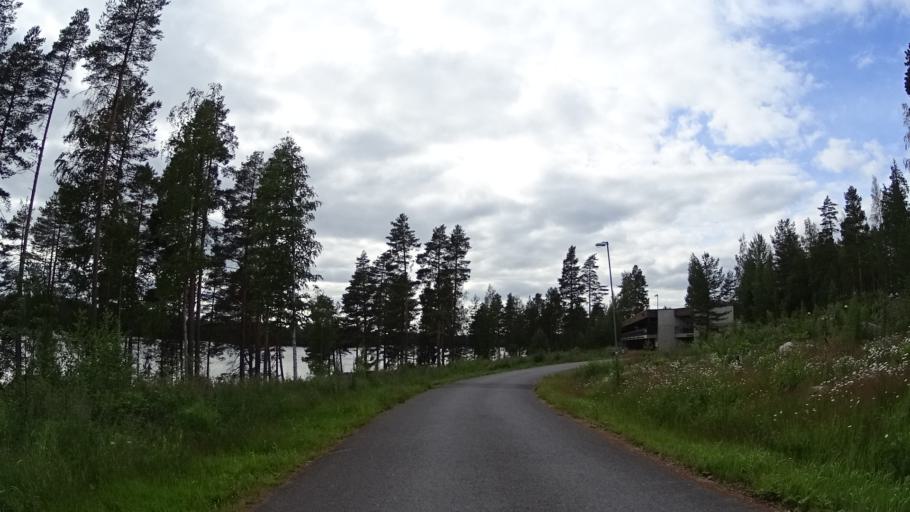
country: FI
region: Southern Ostrobothnia
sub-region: Kuusiokunnat
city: AEhtaeri
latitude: 62.5333
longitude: 24.1844
